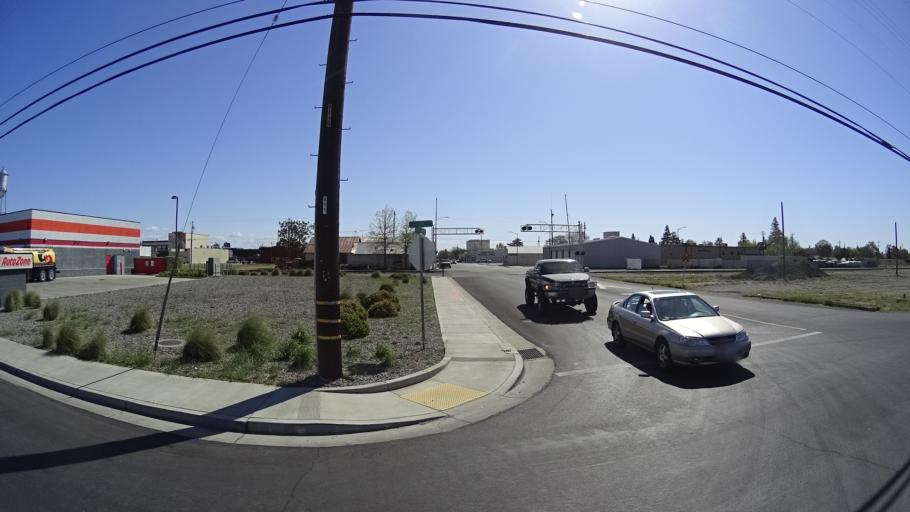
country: US
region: California
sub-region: Glenn County
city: Orland
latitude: 39.7464
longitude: -122.1976
